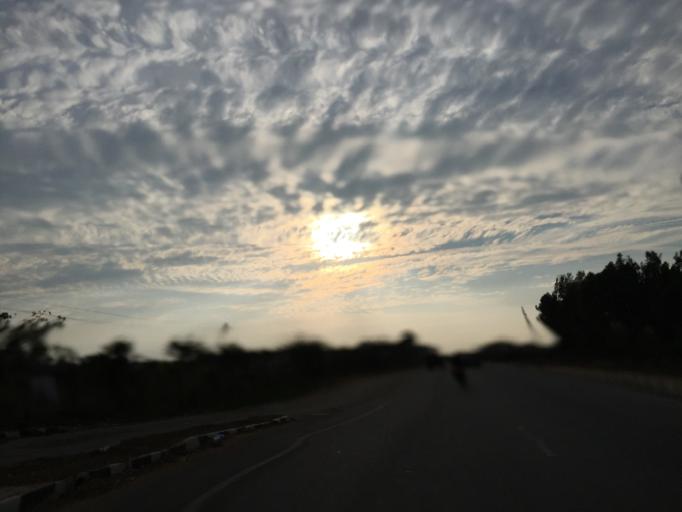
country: IN
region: Karnataka
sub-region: Kolar
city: Kolar
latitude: 13.1402
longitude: 78.2226
